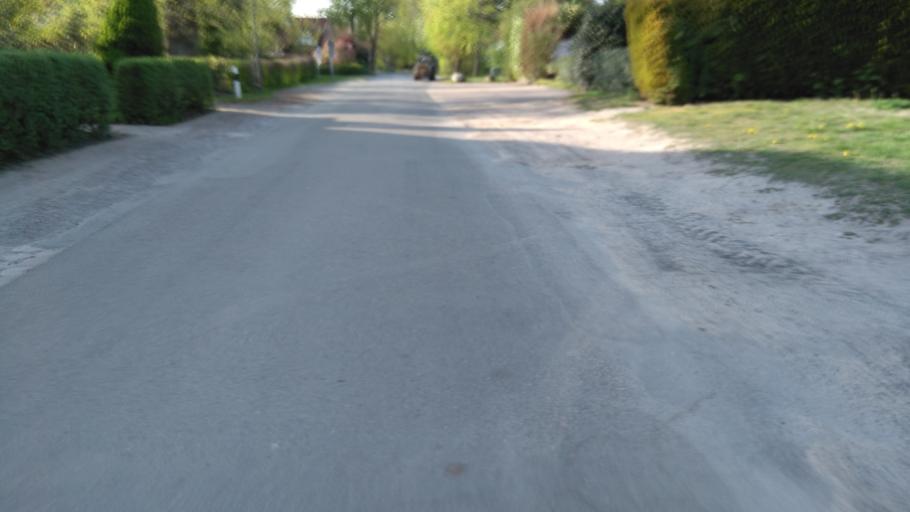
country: DE
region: Lower Saxony
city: Apensen
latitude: 53.4355
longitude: 9.6214
